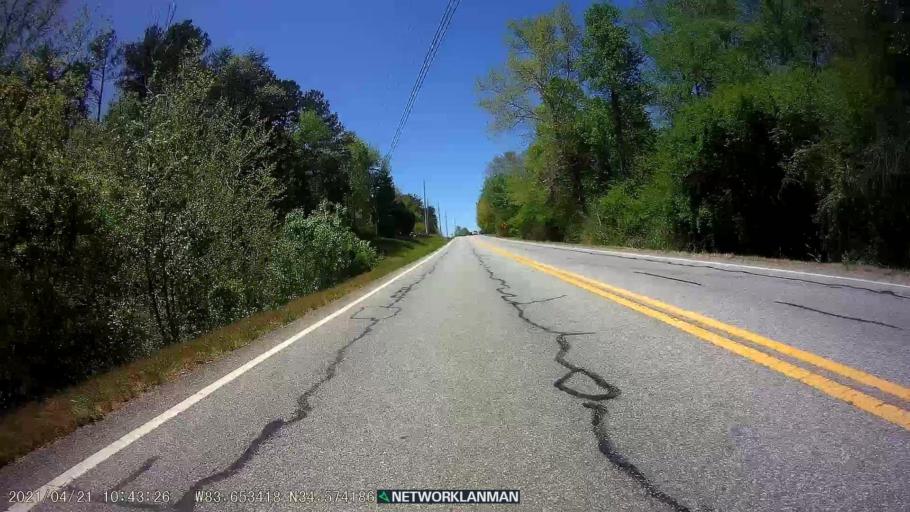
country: US
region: Georgia
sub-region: Habersham County
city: Demorest
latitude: 34.5742
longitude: -83.6528
